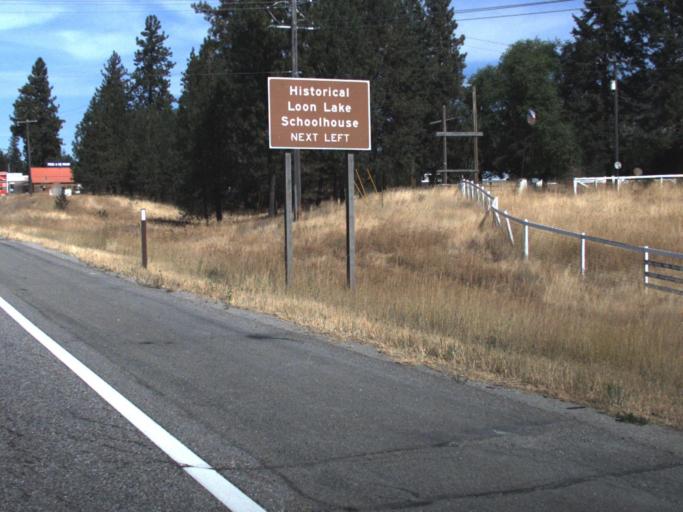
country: US
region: Washington
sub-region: Spokane County
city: Deer Park
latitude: 48.0580
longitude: -117.6192
